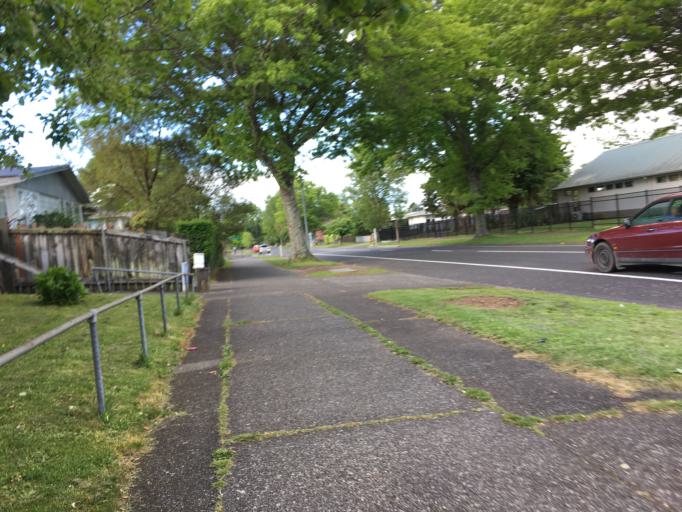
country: NZ
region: Waikato
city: Turangi
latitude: -38.9862
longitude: 175.8118
